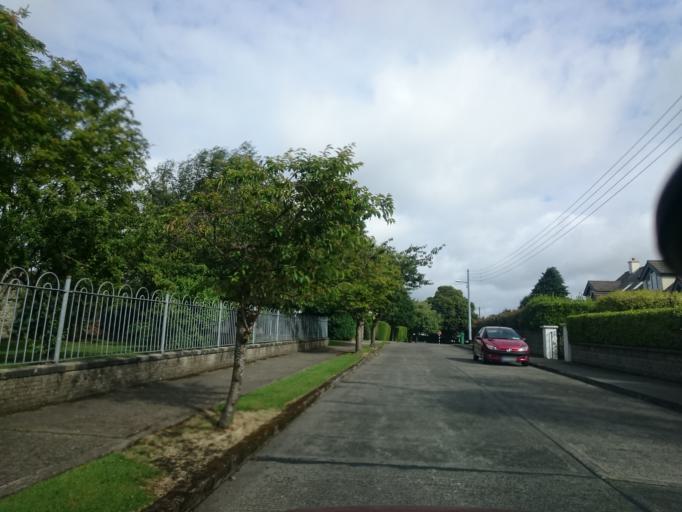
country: IE
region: Leinster
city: Mount Merrion
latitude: 53.2919
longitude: -6.2074
